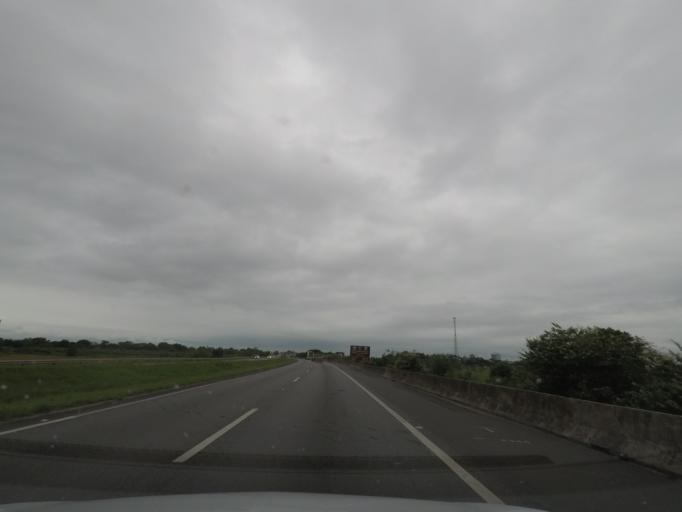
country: BR
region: Sao Paulo
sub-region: Registro
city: Registro
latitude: -24.4827
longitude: -47.8323
